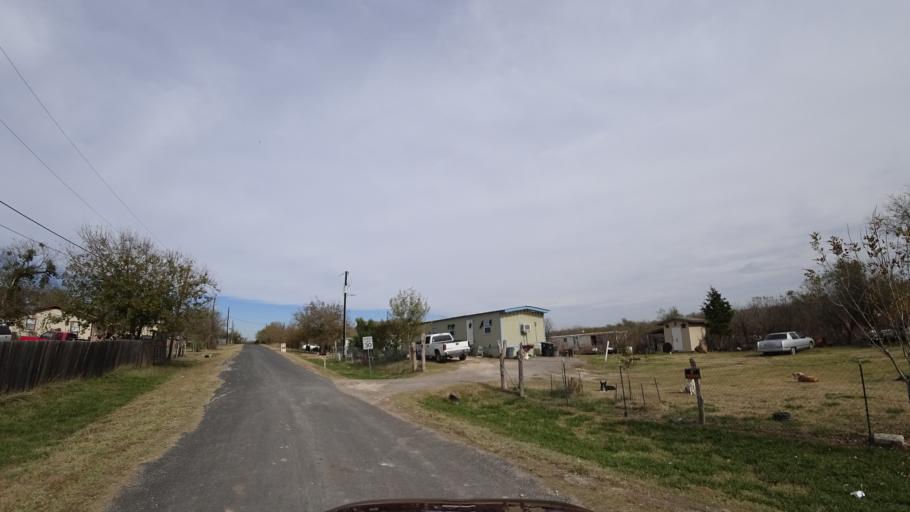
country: US
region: Texas
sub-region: Travis County
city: Garfield
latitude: 30.1265
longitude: -97.6139
